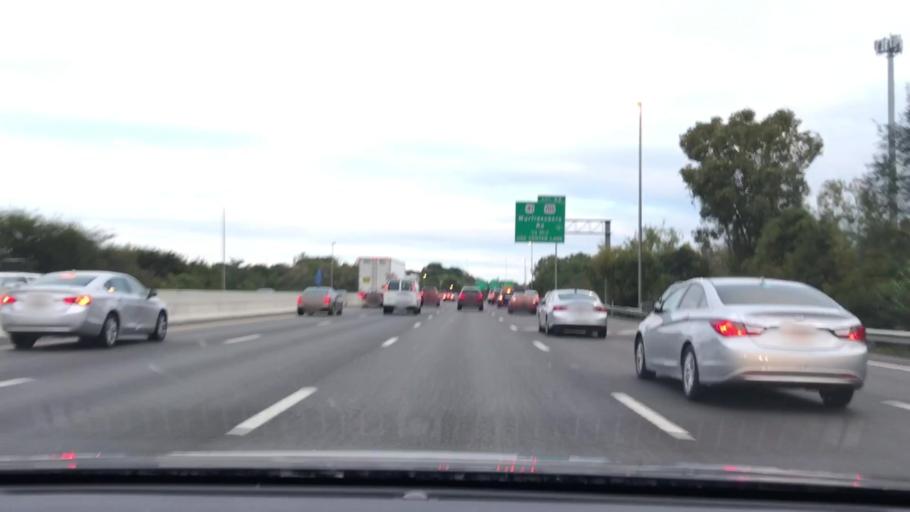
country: US
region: Tennessee
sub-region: Davidson County
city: Oak Hill
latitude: 36.1152
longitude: -86.7247
